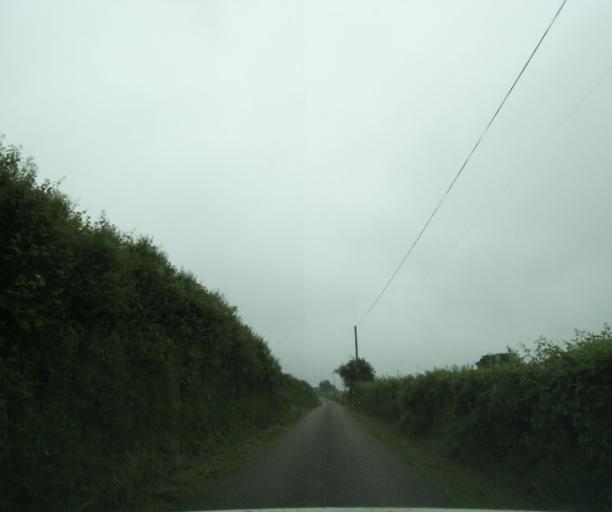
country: FR
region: Bourgogne
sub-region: Departement de Saone-et-Loire
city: Charolles
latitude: 46.4174
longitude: 4.3798
